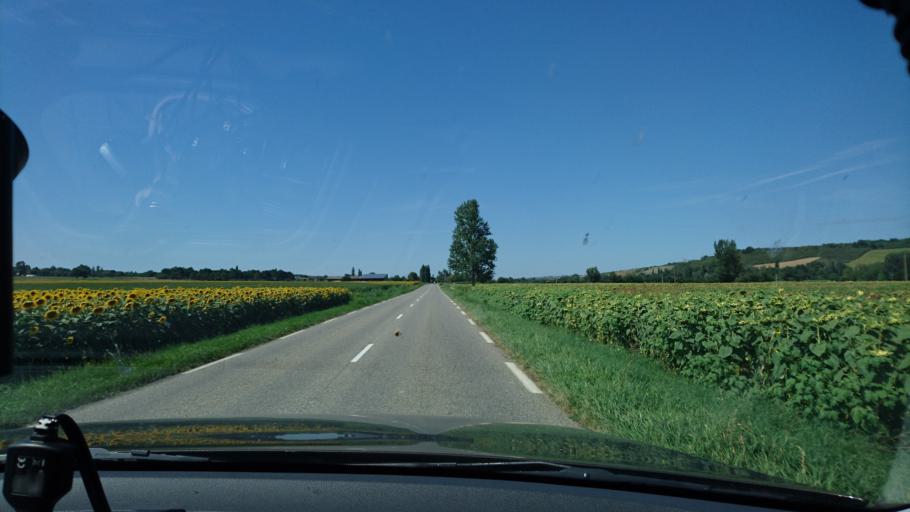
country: FR
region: Midi-Pyrenees
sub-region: Departement de l'Ariege
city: Lezat-sur-Leze
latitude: 43.2510
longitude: 1.3634
